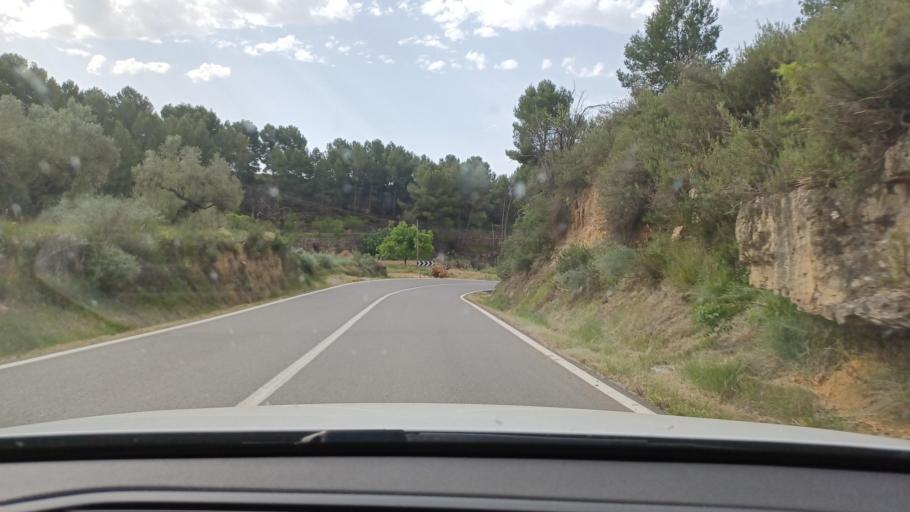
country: ES
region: Catalonia
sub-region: Provincia de Tarragona
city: Bot
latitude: 41.0224
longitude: 0.3821
